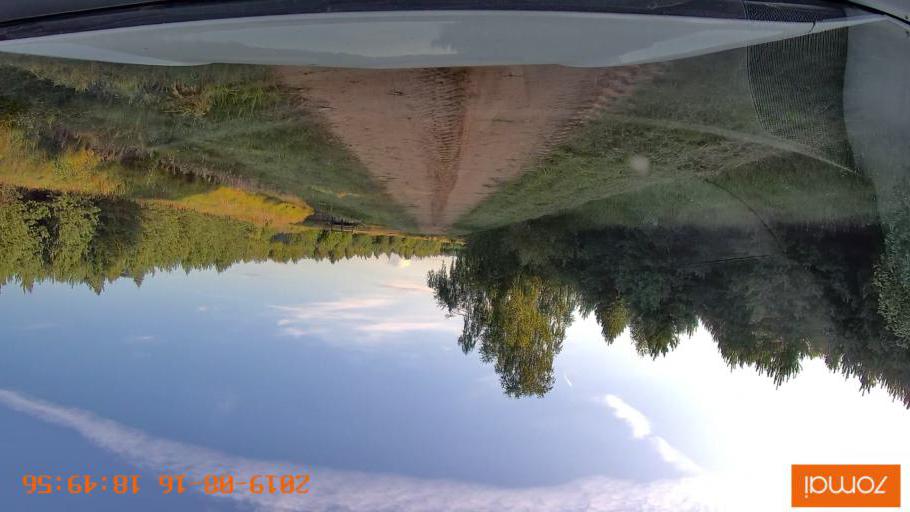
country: BY
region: Mogilev
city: Asipovichy
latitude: 53.2395
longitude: 28.6646
